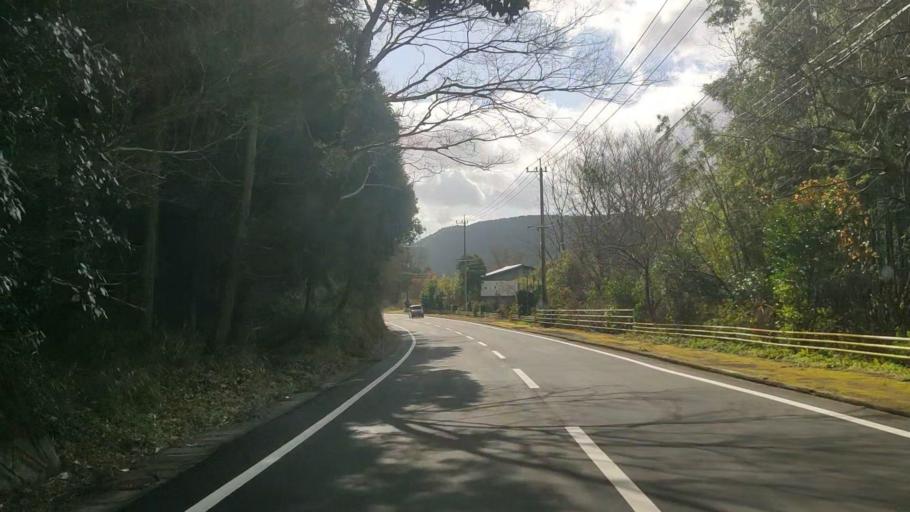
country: JP
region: Kagoshima
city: Okuchi-shinohara
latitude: 31.9861
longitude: 130.7432
